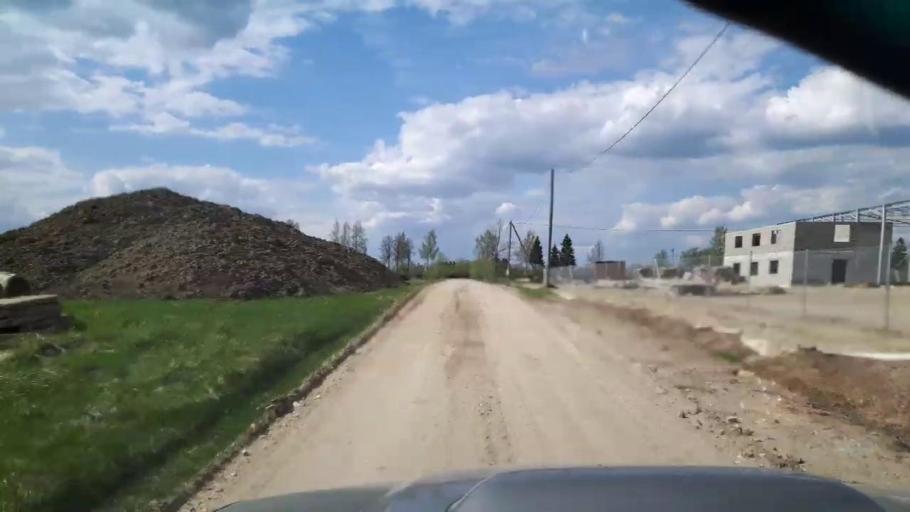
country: EE
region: Paernumaa
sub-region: Sindi linn
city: Sindi
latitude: 58.4262
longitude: 24.7272
